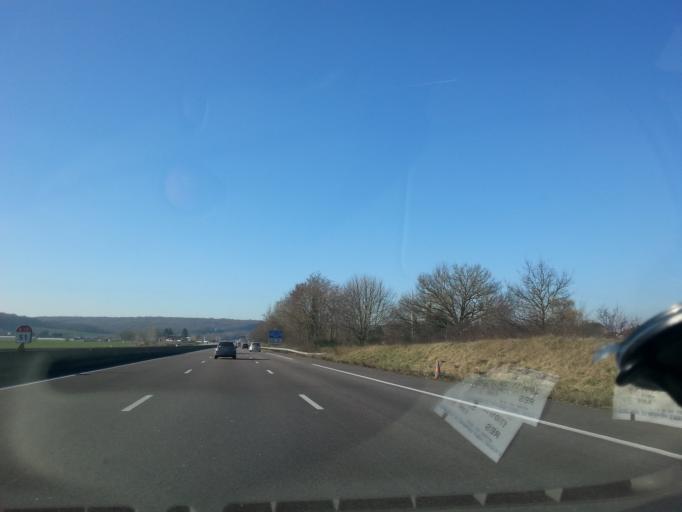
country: FR
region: Ile-de-France
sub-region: Departement des Yvelines
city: Rosny-sur-Seine
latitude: 48.9910
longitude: 1.6435
